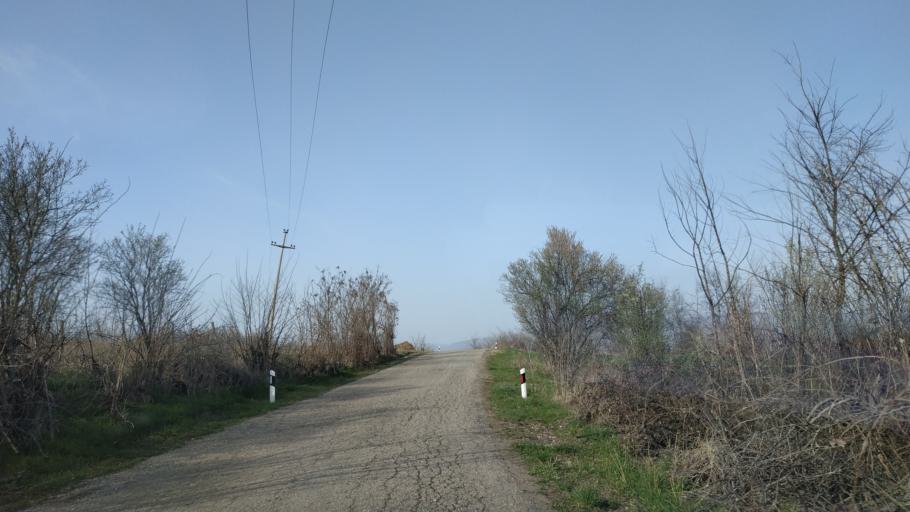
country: RS
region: Central Serbia
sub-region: Nisavski Okrug
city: Aleksinac
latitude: 43.5133
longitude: 21.6476
